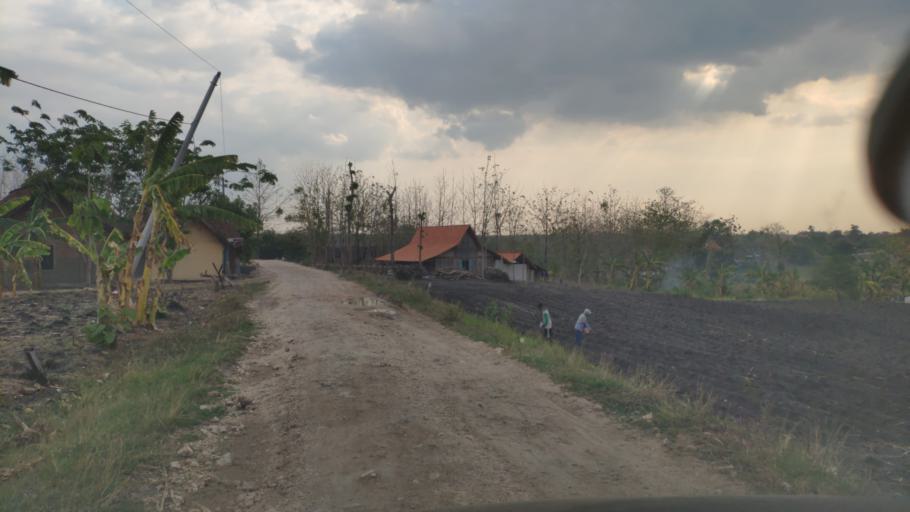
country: ID
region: Central Java
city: Randublatung
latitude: -7.2849
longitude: 111.2755
